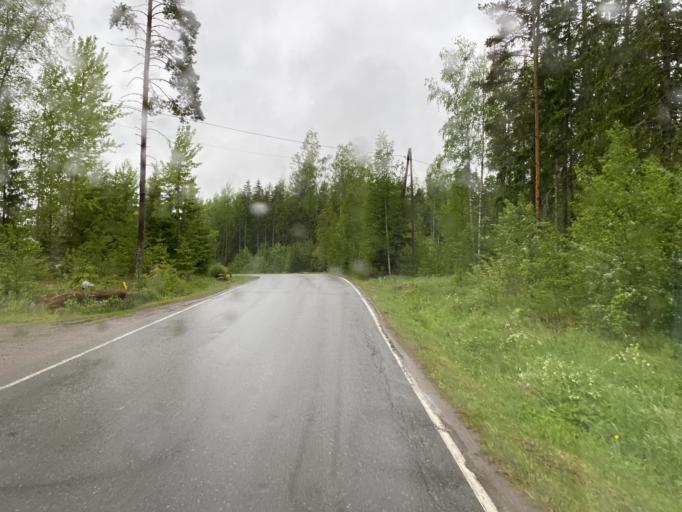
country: FI
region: Pirkanmaa
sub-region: Etelae-Pirkanmaa
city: Urjala
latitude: 60.9696
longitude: 23.5273
